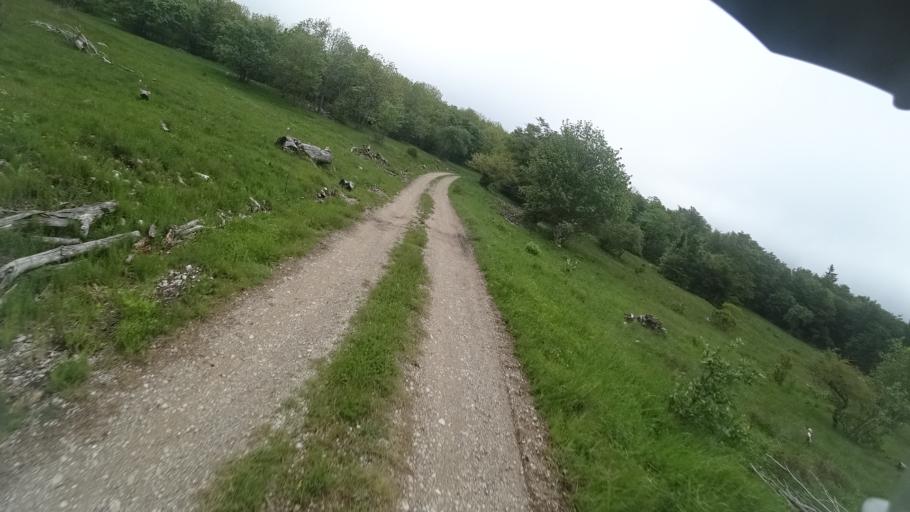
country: BA
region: Federation of Bosnia and Herzegovina
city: Bihac
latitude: 44.7017
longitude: 15.8266
